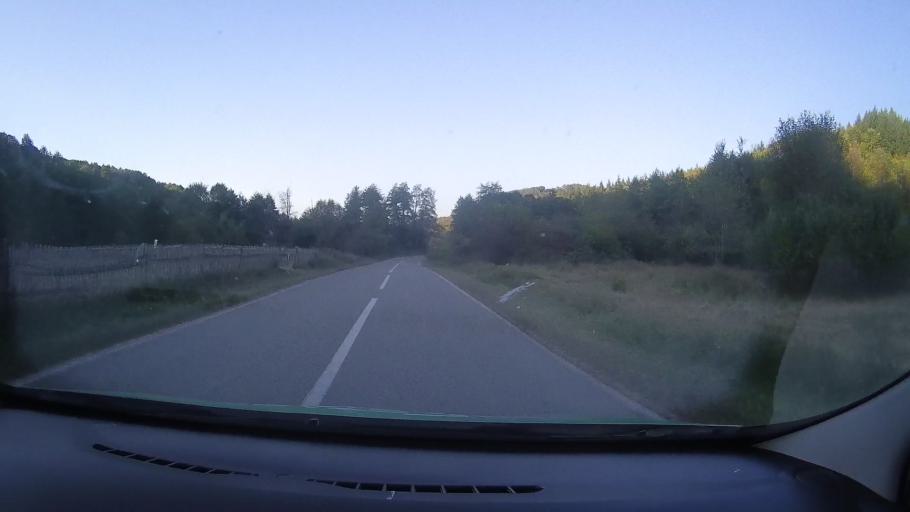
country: RO
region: Timis
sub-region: Comuna Fardea
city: Fardea
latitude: 45.7044
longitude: 22.1604
